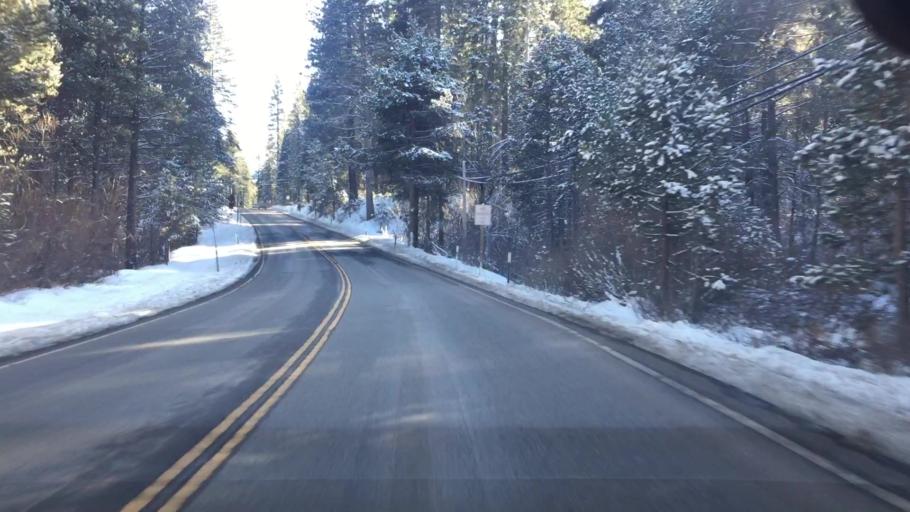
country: US
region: California
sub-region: Placer County
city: Tahoma
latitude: 39.0512
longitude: -120.1182
